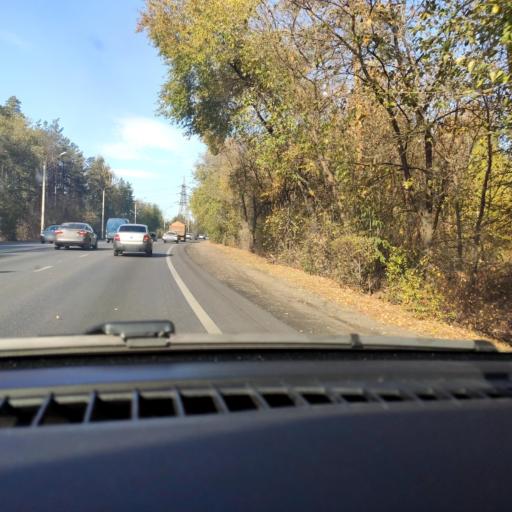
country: RU
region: Voronezj
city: Pridonskoy
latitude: 51.6770
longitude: 39.1151
